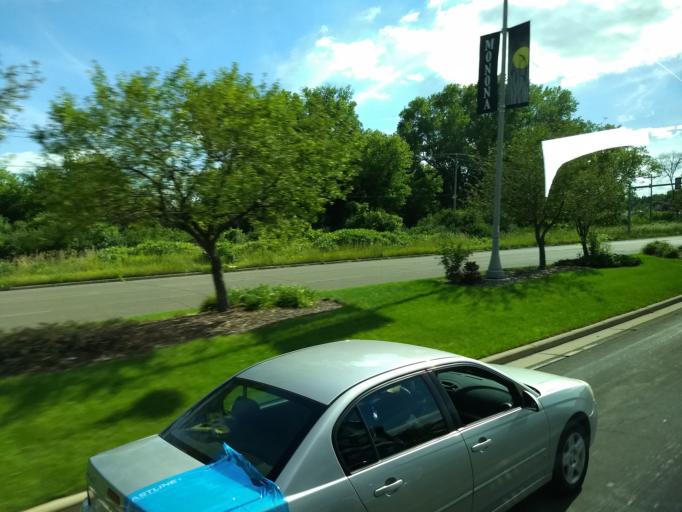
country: US
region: Wisconsin
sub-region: Dane County
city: Monona
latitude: 43.0482
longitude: -89.3098
